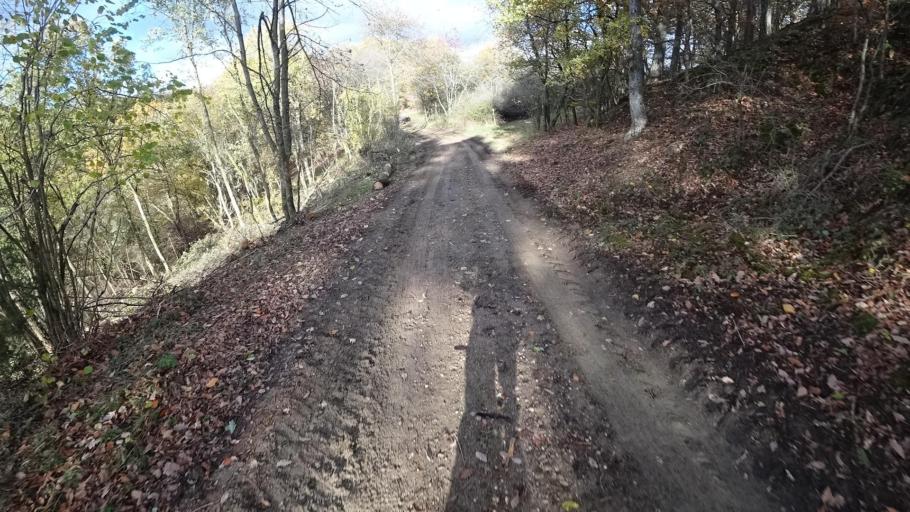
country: DE
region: Rheinland-Pfalz
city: Honningen
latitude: 50.4698
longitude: 6.9400
